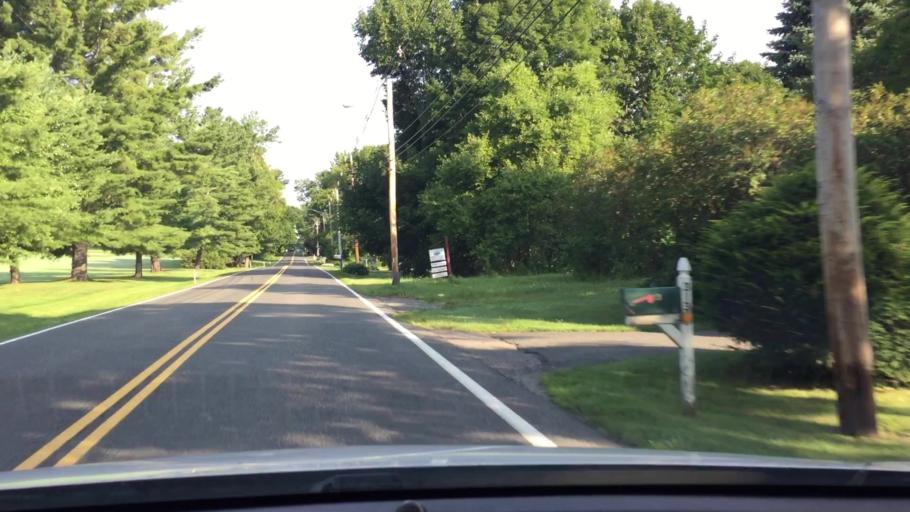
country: US
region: Massachusetts
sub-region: Berkshire County
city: Lenox
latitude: 42.3433
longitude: -73.2618
